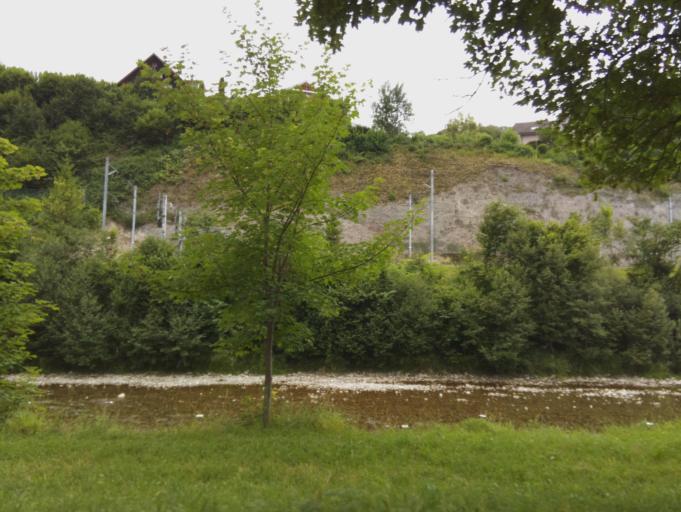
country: CH
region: Saint Gallen
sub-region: Wahlkreis Toggenburg
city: Lichtensteig
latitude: 47.3147
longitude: 9.0798
